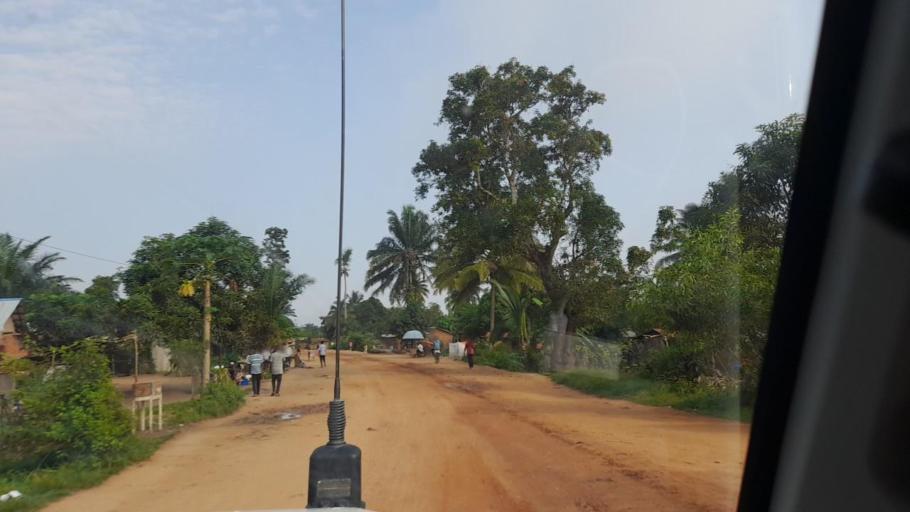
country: CD
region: Kasai-Occidental
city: Kananga
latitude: -5.8917
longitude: 22.3753
